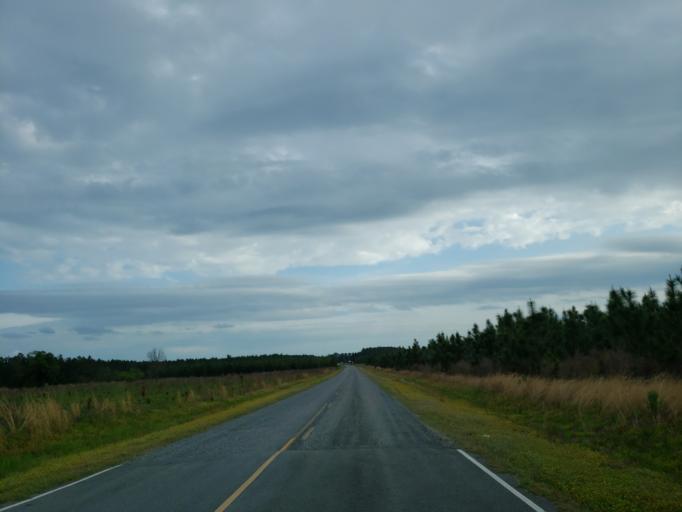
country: US
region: Georgia
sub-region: Dooly County
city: Vienna
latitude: 32.1146
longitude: -83.7559
